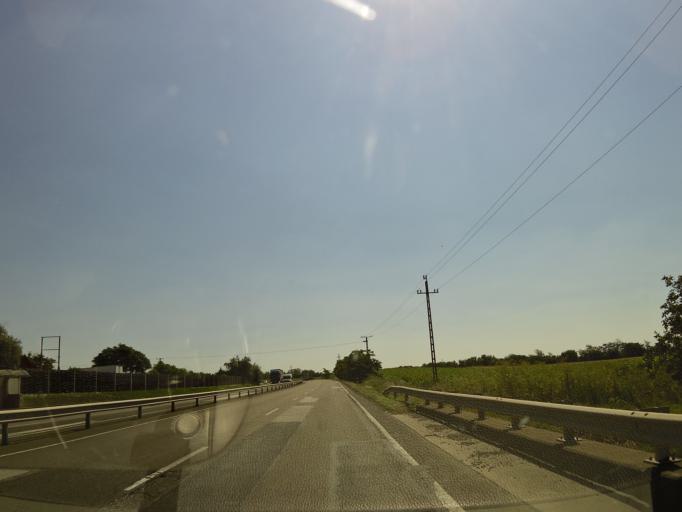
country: HU
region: Jasz-Nagykun-Szolnok
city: Szajol
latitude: 47.1758
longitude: 20.3090
